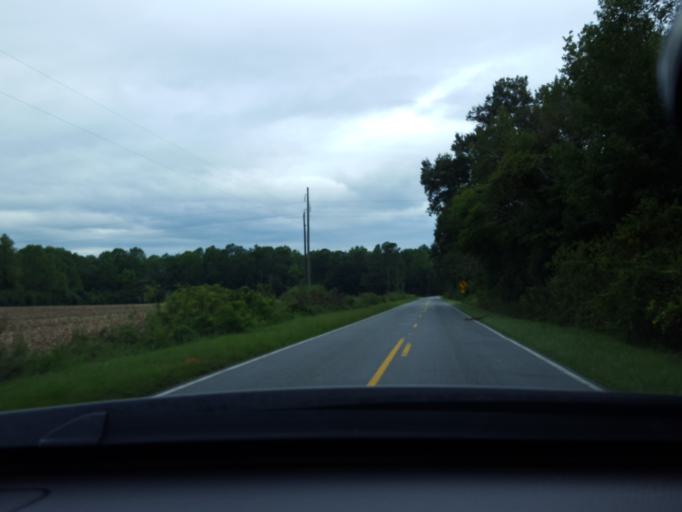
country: US
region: North Carolina
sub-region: Sampson County
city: Roseboro
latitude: 34.7848
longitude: -78.3697
